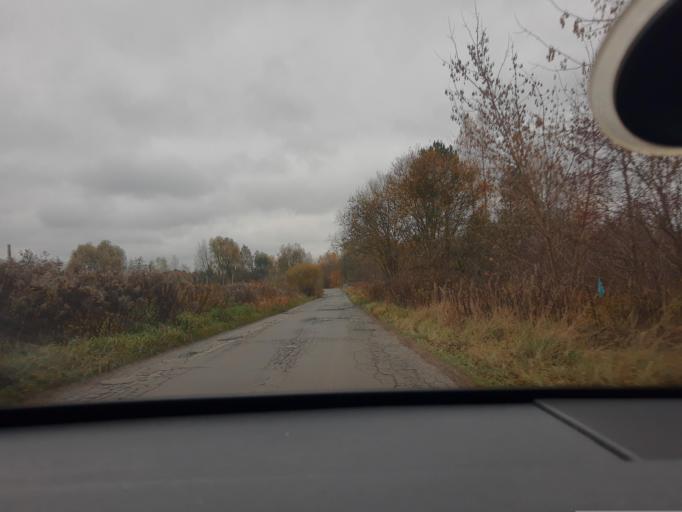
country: PL
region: Lodz Voivodeship
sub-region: Powiat pabianicki
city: Konstantynow Lodzki
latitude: 51.7486
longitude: 19.3719
